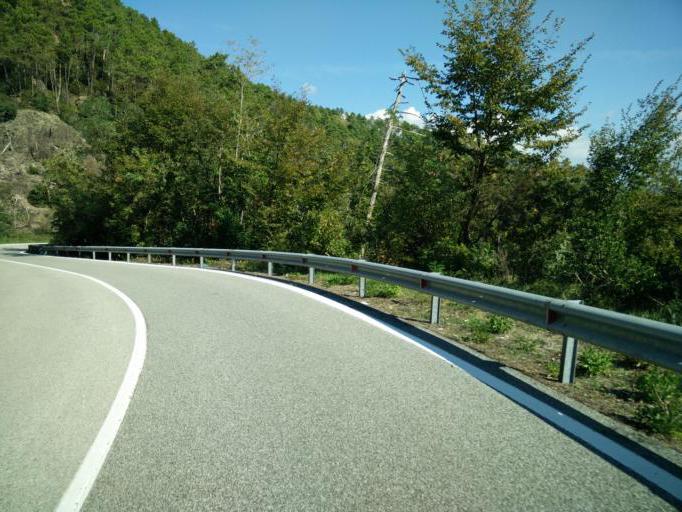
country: IT
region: Liguria
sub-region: Provincia di La Spezia
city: Framura
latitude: 44.2478
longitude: 9.5964
